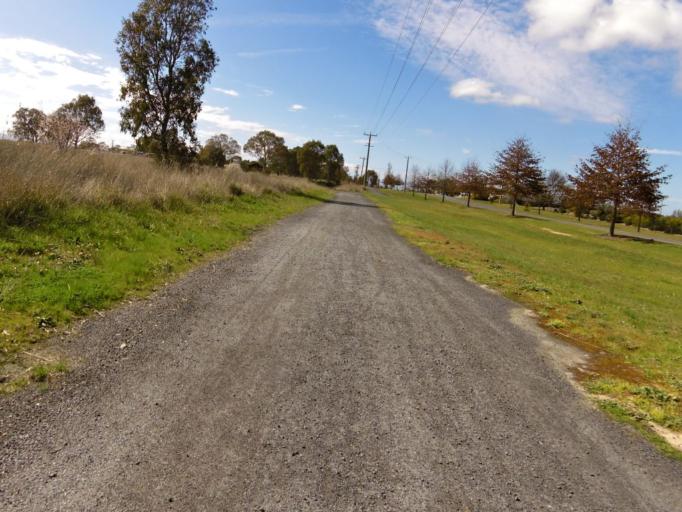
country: AU
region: Victoria
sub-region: Mansfield
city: Mansfield
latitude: -37.0493
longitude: 146.0691
